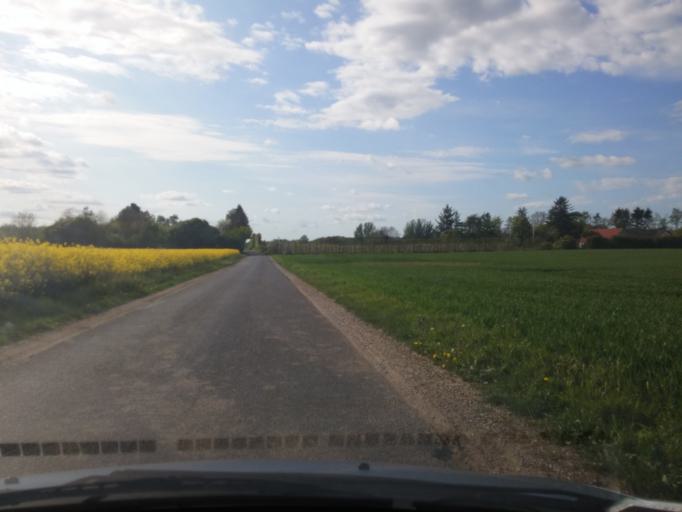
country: DK
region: South Denmark
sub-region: Nyborg Kommune
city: Ullerslev
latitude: 55.3669
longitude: 10.6569
